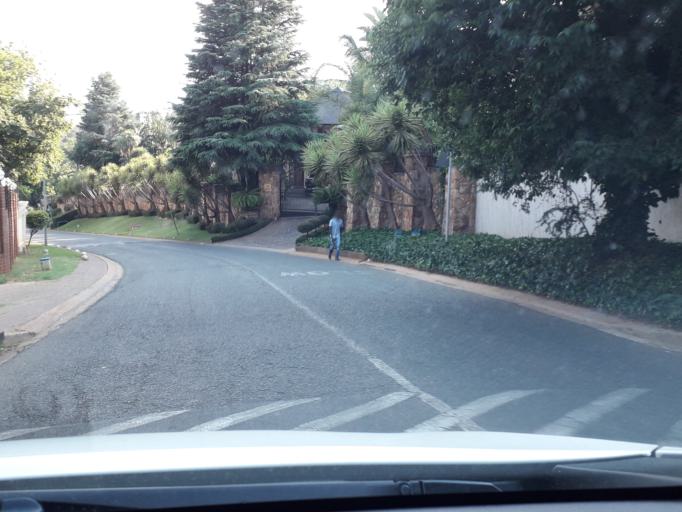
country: ZA
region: Gauteng
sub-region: City of Johannesburg Metropolitan Municipality
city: Roodepoort
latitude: -26.1510
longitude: 27.9594
